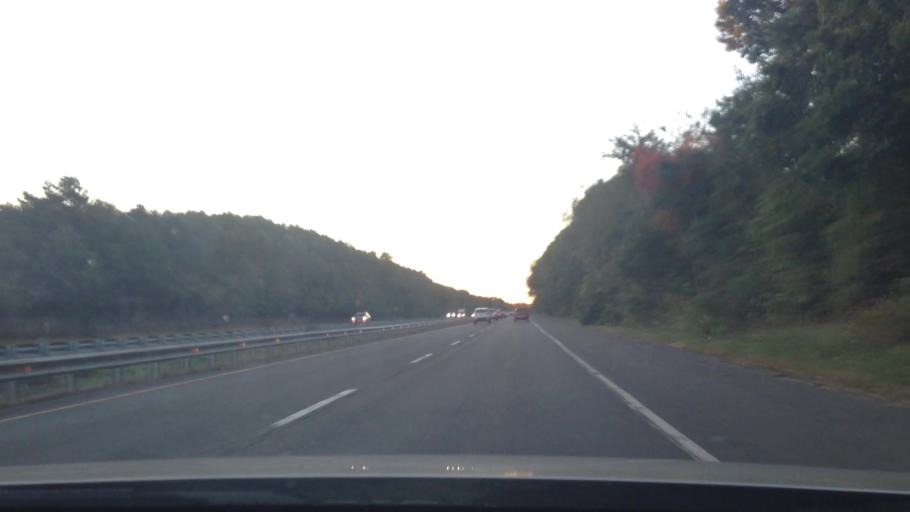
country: US
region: New York
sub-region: Suffolk County
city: Coram
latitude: 40.9059
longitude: -73.0056
